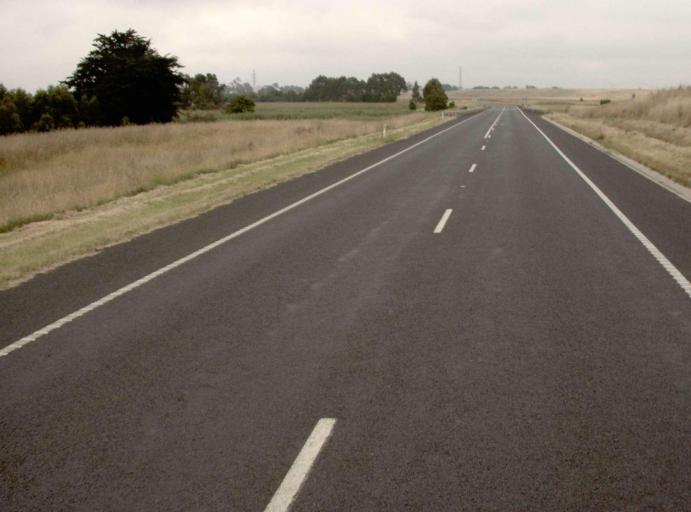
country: AU
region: Victoria
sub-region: Latrobe
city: Morwell
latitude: -38.2720
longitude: 146.3266
